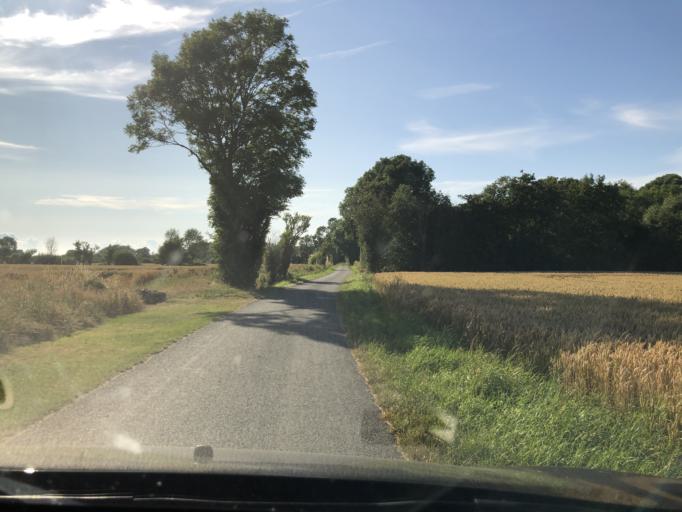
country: DK
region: South Denmark
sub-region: AEro Kommune
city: AEroskobing
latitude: 54.8542
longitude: 10.3678
